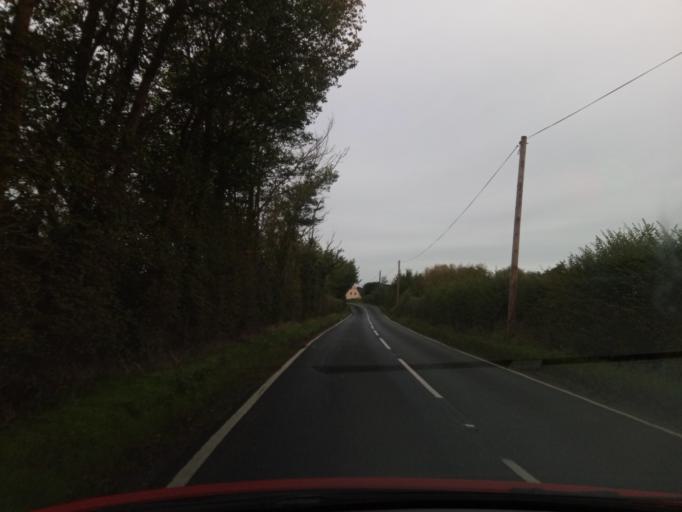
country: GB
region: England
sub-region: Essex
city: West Mersea
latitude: 51.8072
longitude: 0.8998
